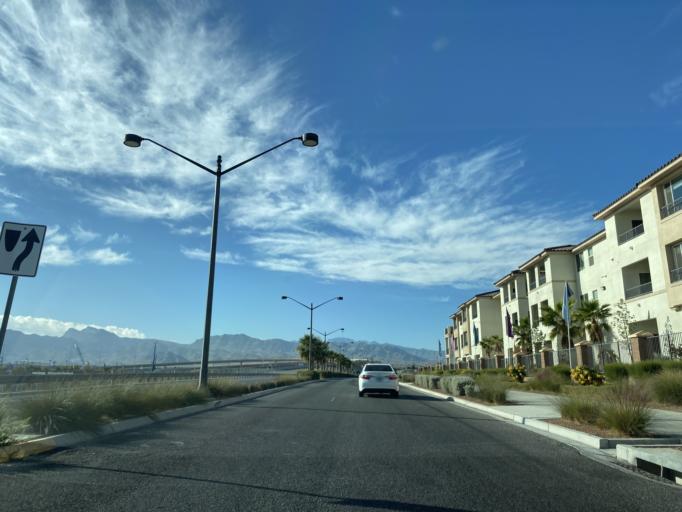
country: US
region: Nevada
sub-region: Clark County
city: Las Vegas
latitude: 36.2772
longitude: -115.2540
